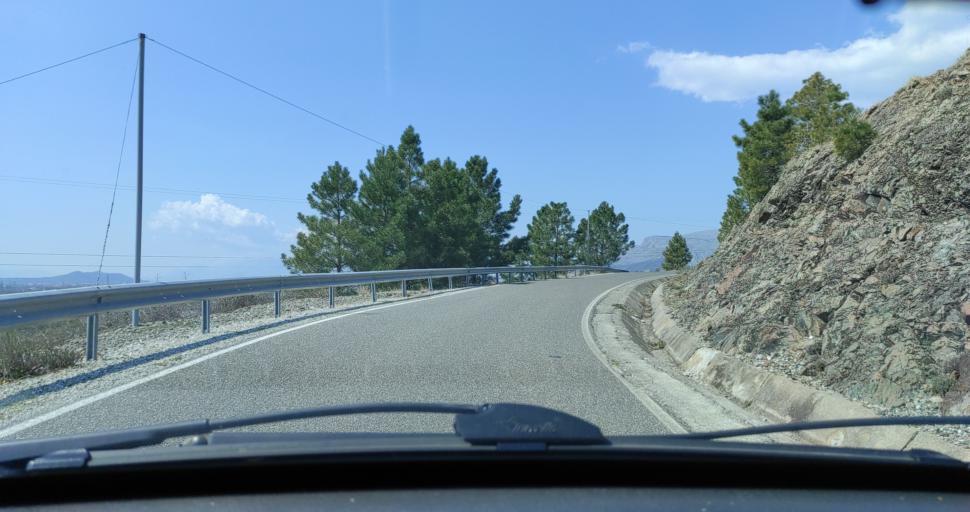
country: AL
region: Shkoder
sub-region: Rrethi i Shkodres
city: Hajmel
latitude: 41.9825
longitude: 19.6445
